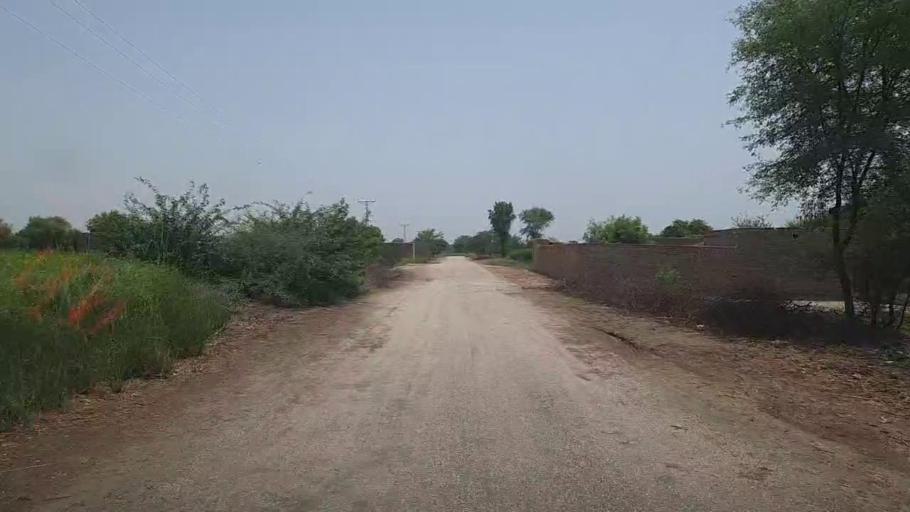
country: PK
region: Sindh
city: Pad Idan
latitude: 26.8363
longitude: 68.3248
